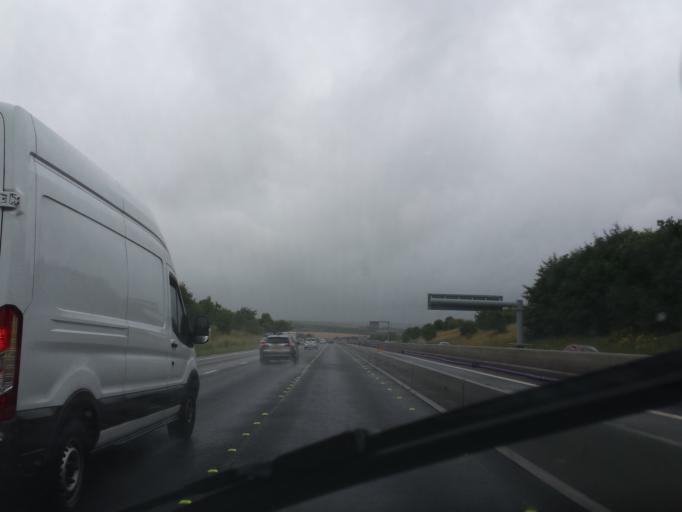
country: GB
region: England
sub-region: Derbyshire
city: Barlborough
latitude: 53.2745
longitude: -1.3018
